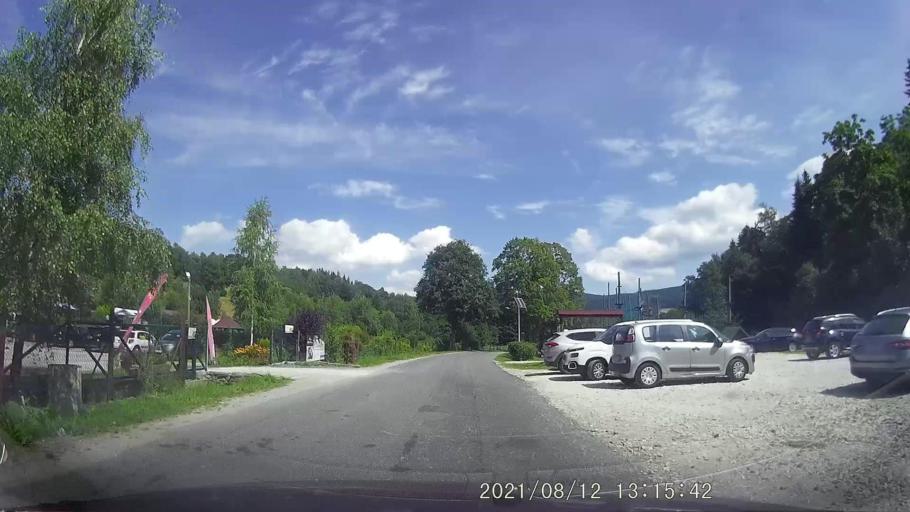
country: PL
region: Lower Silesian Voivodeship
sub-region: Powiat klodzki
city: Stronie Slaskie
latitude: 50.2620
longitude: 16.8707
